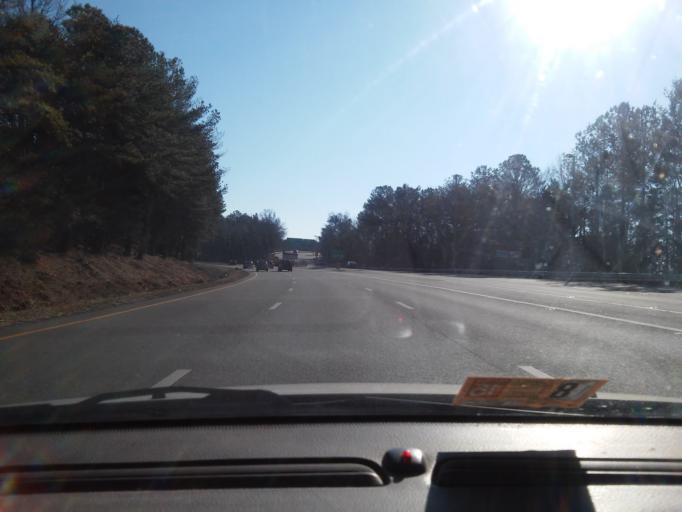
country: US
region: Virginia
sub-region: Henrico County
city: Lakeside
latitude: 37.5881
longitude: -77.4784
